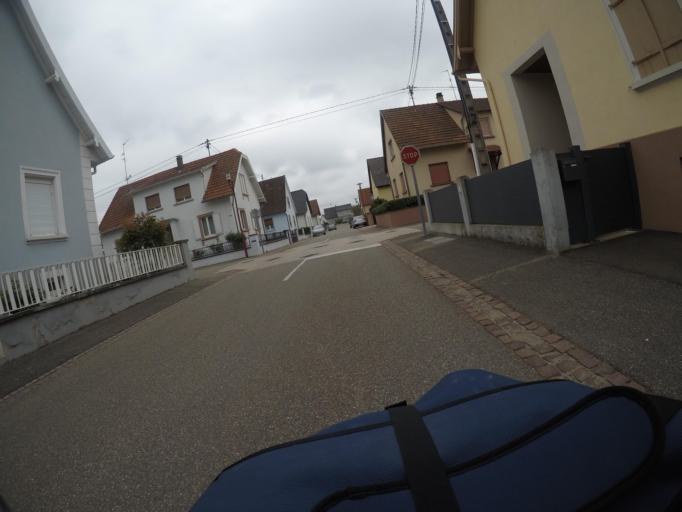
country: FR
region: Alsace
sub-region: Departement du Bas-Rhin
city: Drusenheim
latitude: 48.7573
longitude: 7.9510
